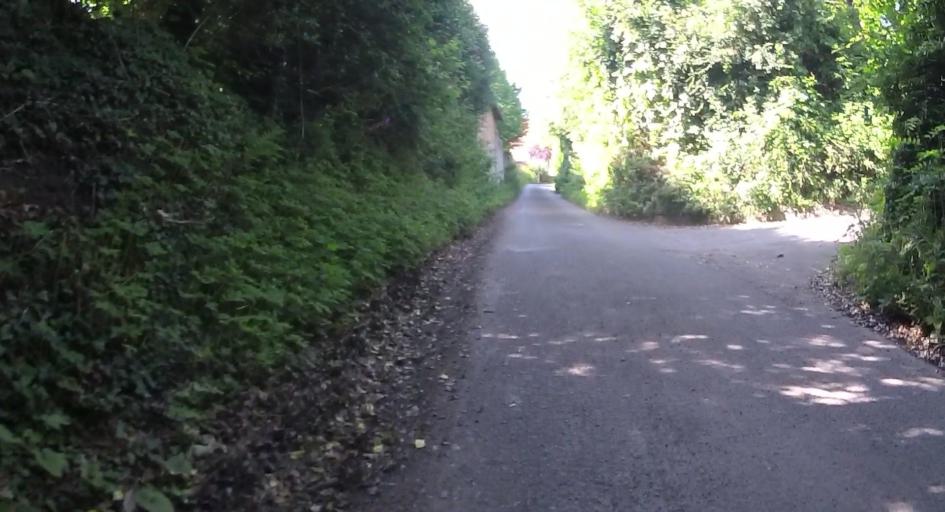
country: GB
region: England
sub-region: Hampshire
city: Kingsley
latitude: 51.1616
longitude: -0.8974
